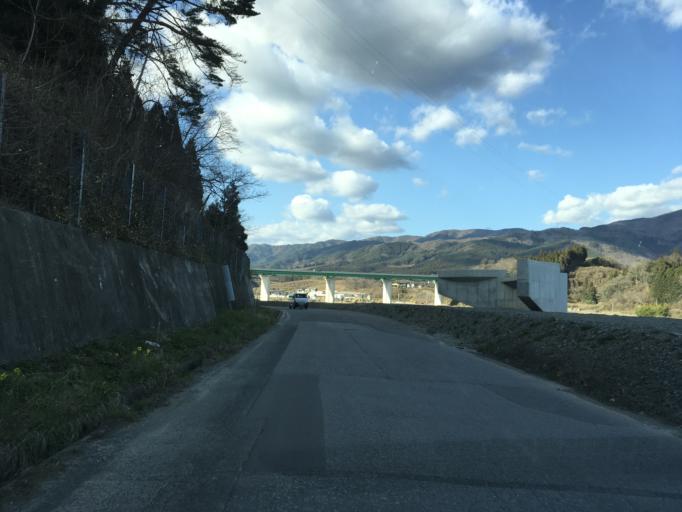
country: JP
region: Iwate
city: Ofunato
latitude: 39.0226
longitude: 141.6164
